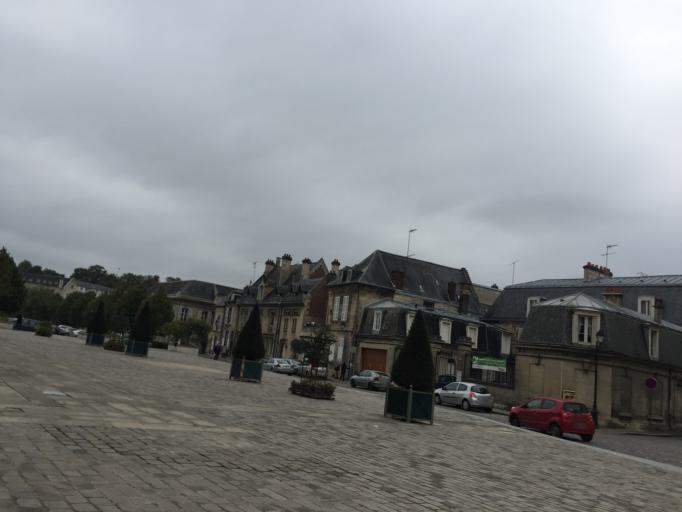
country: FR
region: Picardie
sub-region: Departement de l'Aisne
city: Soissons
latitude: 49.3811
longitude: 3.3246
